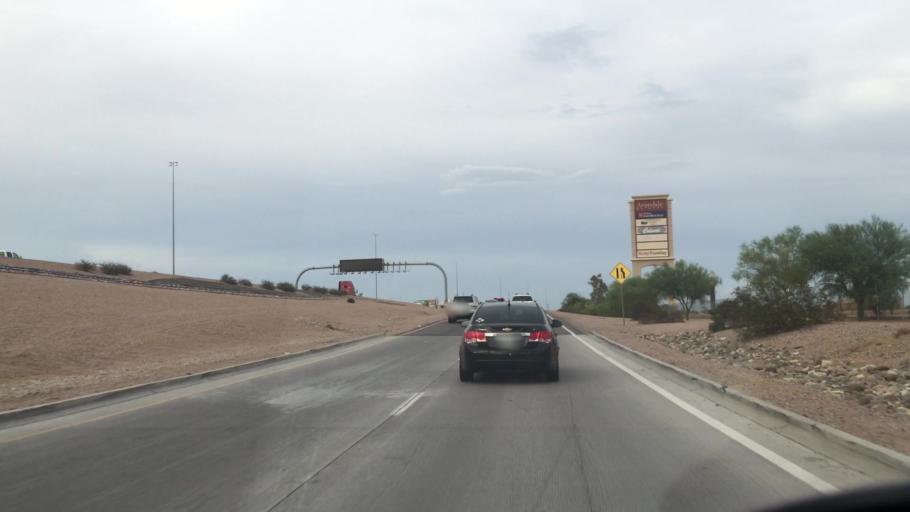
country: US
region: Arizona
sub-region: Maricopa County
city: Tolleson
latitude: 33.4588
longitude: -112.3060
